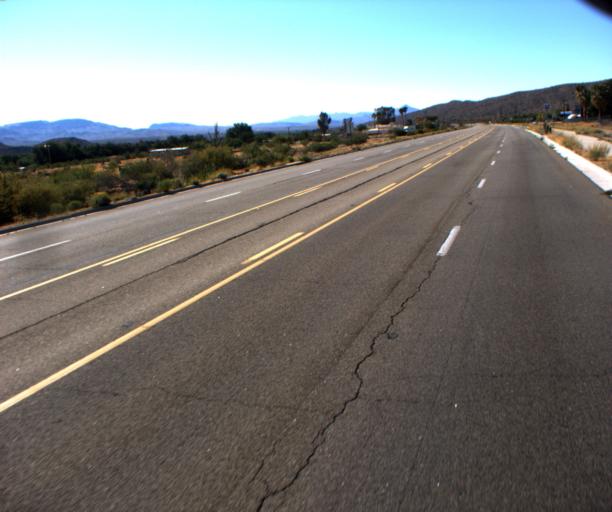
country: US
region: Arizona
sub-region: Yavapai County
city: Bagdad
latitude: 34.7076
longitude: -113.6127
